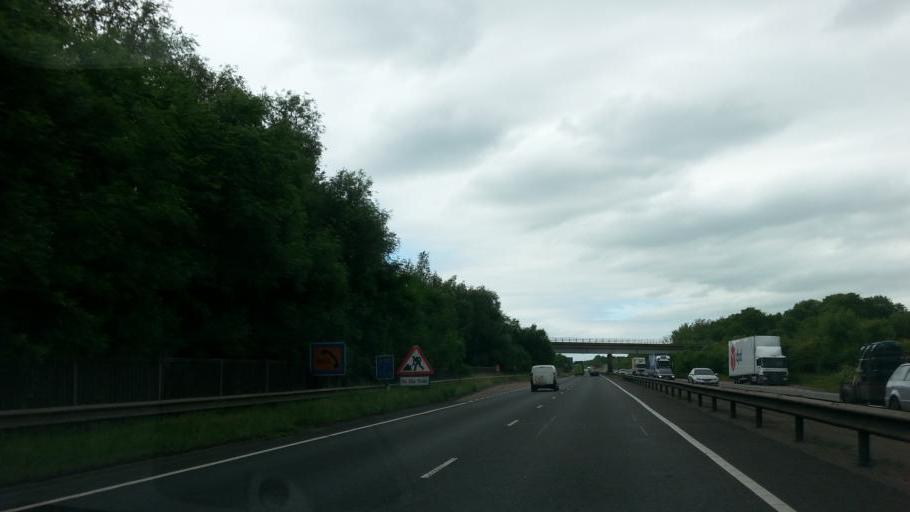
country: GB
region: England
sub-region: Leicestershire
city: Ashby de la Zouch
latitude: 52.7415
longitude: -1.4573
